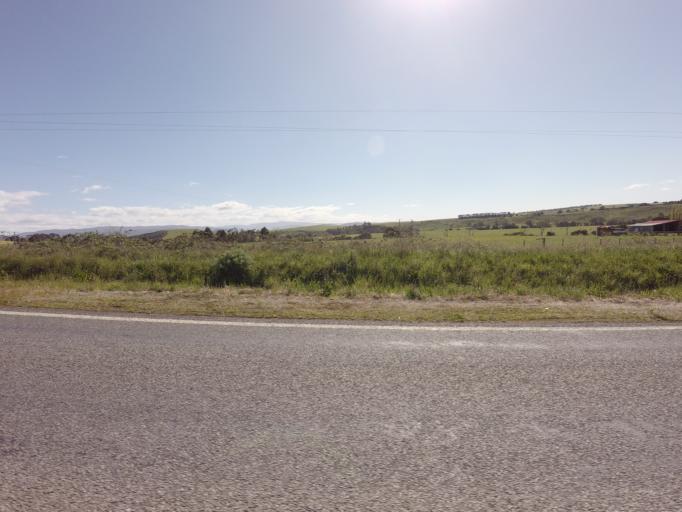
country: AU
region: Tasmania
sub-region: Derwent Valley
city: New Norfolk
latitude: -42.6917
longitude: 146.9410
